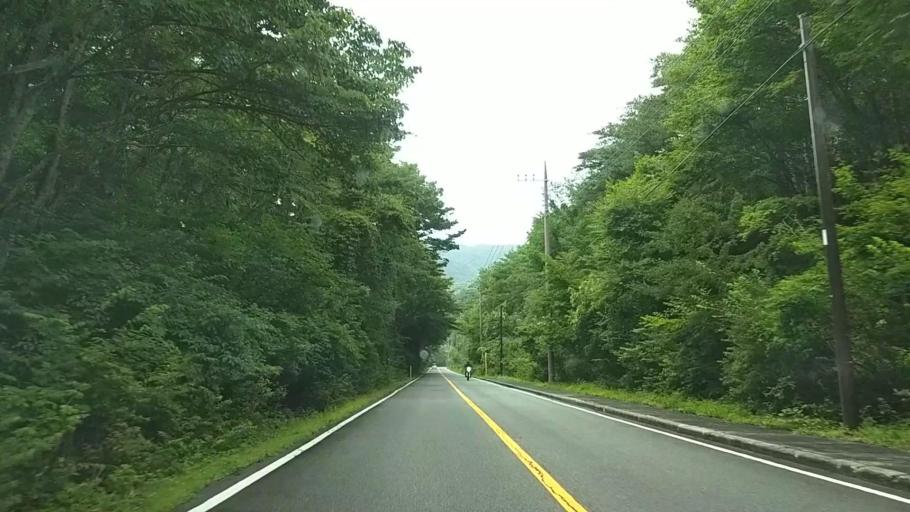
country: JP
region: Yamanashi
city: Fujikawaguchiko
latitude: 35.4688
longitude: 138.5991
